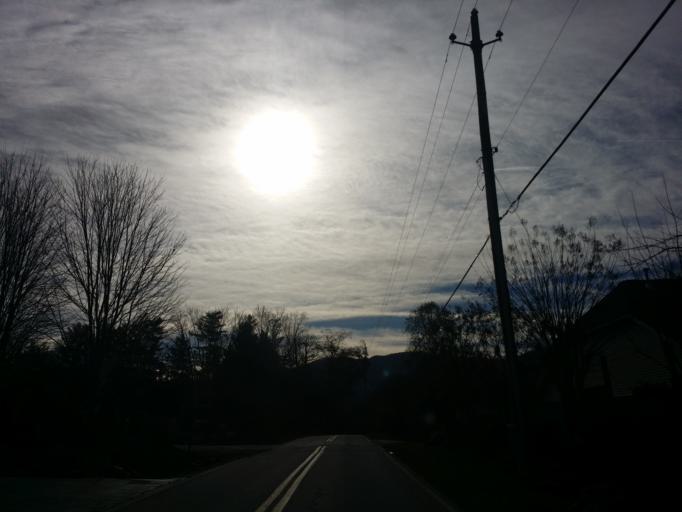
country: US
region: North Carolina
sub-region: Buncombe County
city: Swannanoa
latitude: 35.6181
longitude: -82.4282
